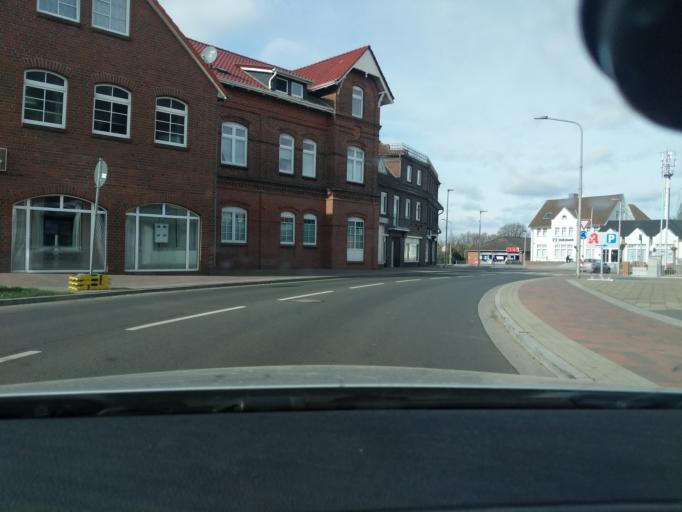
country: DE
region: Lower Saxony
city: Drochtersen
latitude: 53.7092
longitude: 9.3853
